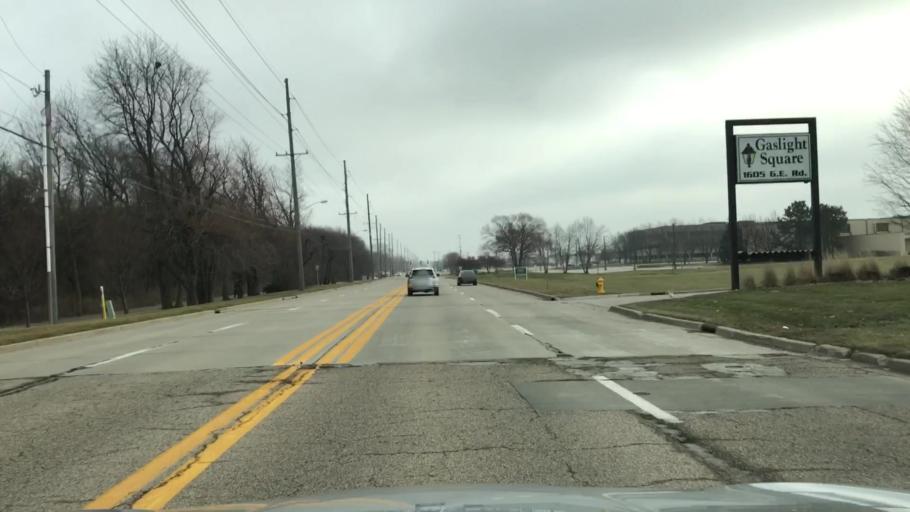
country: US
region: Illinois
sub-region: McLean County
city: Normal
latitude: 40.5027
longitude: -88.9443
